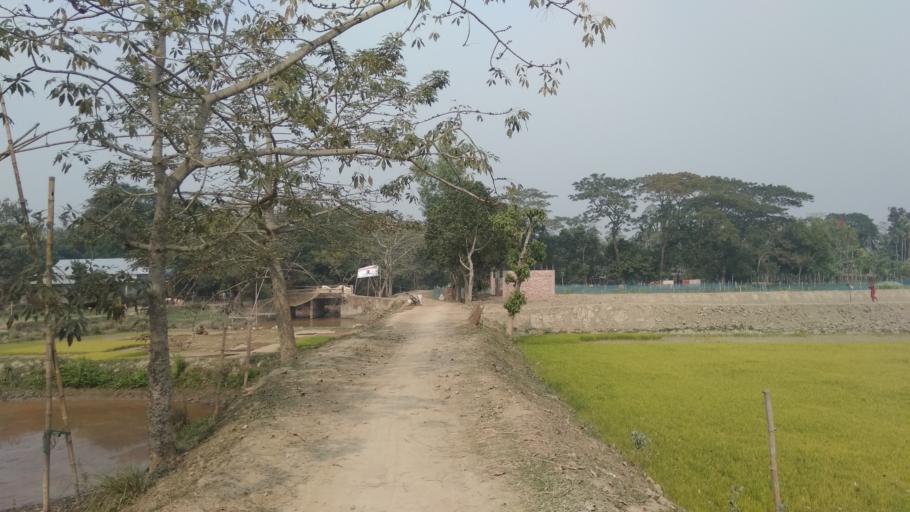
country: BD
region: Dhaka
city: Netrakona
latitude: 24.8901
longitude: 90.6650
